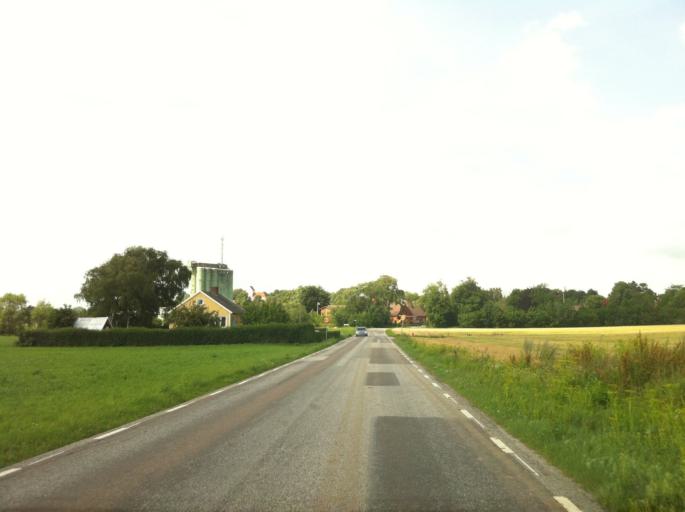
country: SE
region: Skane
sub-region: Lunds Kommun
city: Genarp
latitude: 55.5150
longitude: 13.4141
